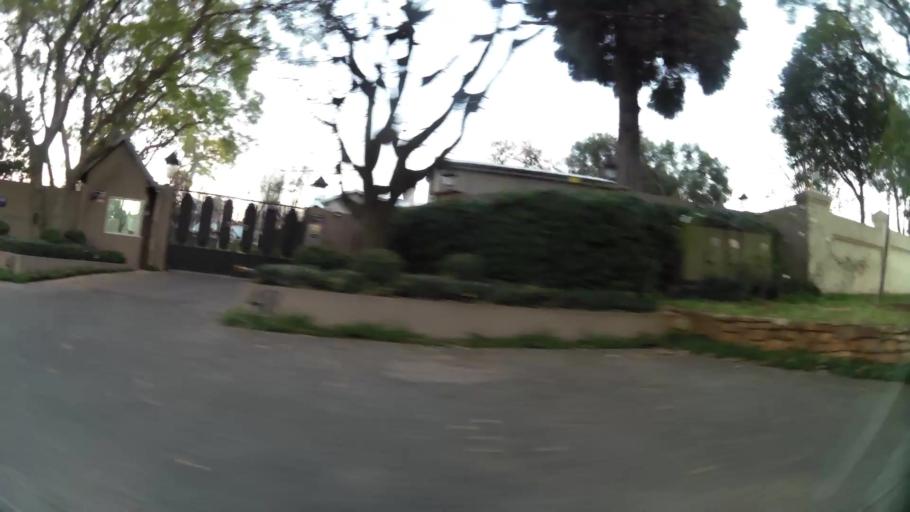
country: ZA
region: Gauteng
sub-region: City of Johannesburg Metropolitan Municipality
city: Johannesburg
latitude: -26.1450
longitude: 28.0537
